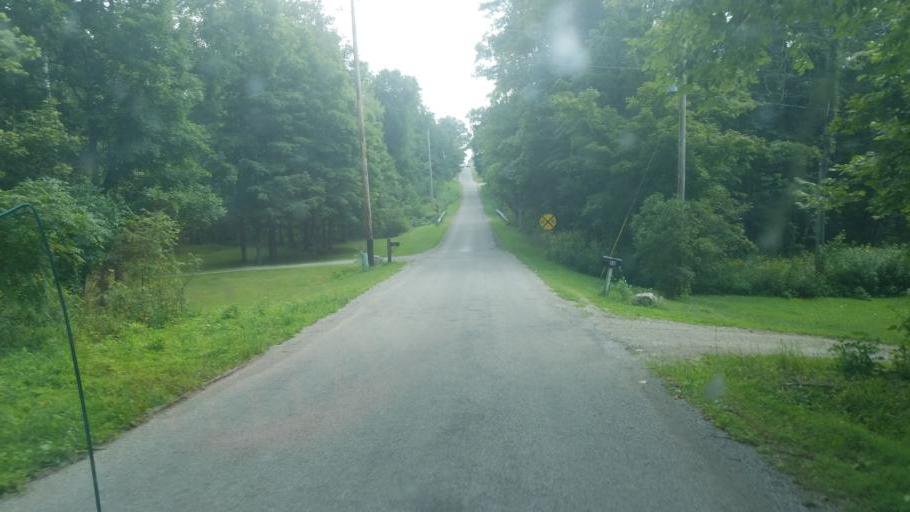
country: US
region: Ohio
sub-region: Huron County
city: New London
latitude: 41.0577
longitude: -82.3756
